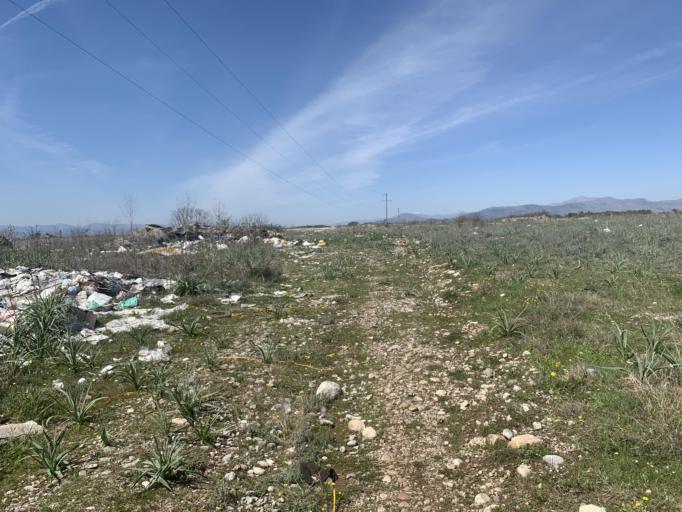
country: AL
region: Shkoder
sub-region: Rrethi i Malesia e Madhe
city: Koplik
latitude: 42.2300
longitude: 19.4352
